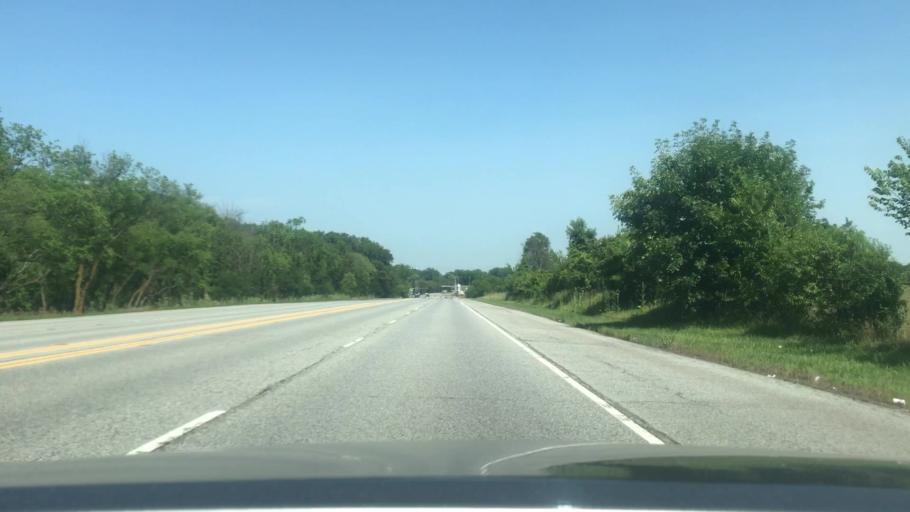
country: US
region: Illinois
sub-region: Cook County
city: Oak Forest
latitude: 41.6035
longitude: -87.7243
